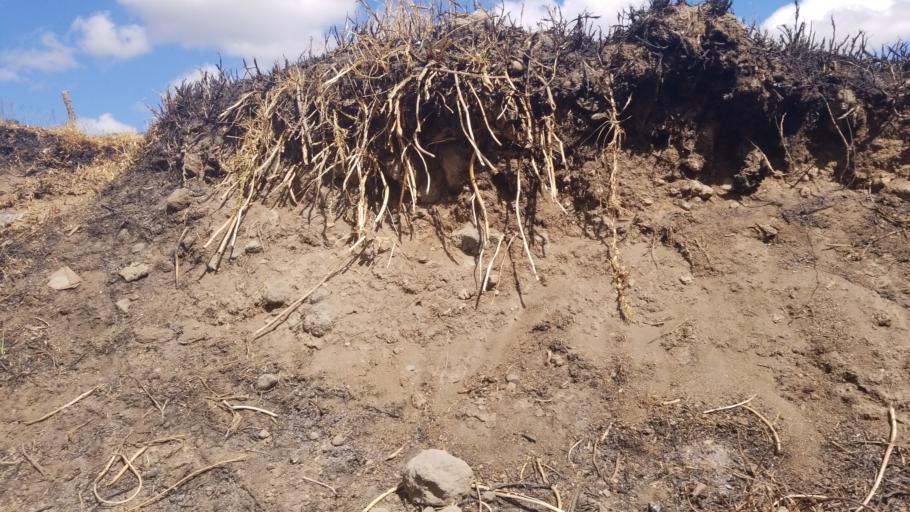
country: GT
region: Quetzaltenango
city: Almolonga
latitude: 14.7868
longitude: -91.5461
